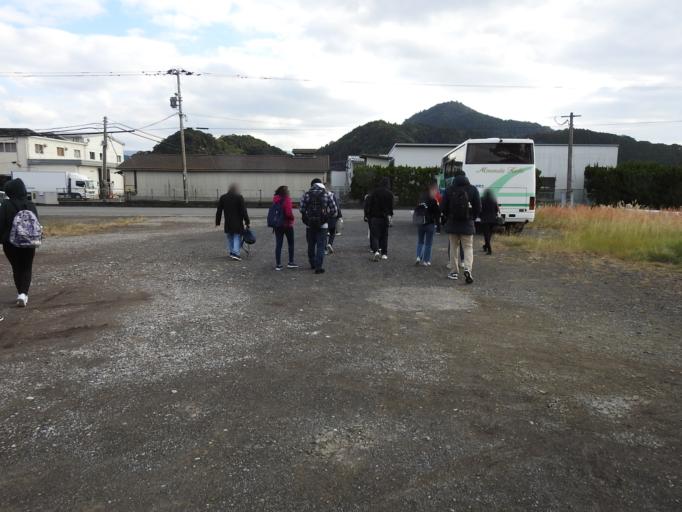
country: JP
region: Kumamoto
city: Minamata
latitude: 32.3004
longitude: 130.4840
